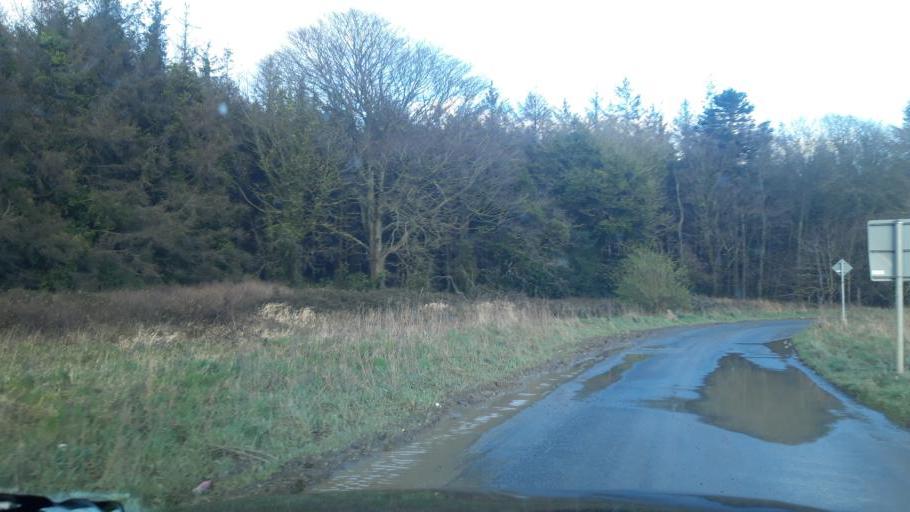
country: IE
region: Leinster
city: Portraine
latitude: 53.4889
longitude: -6.1280
